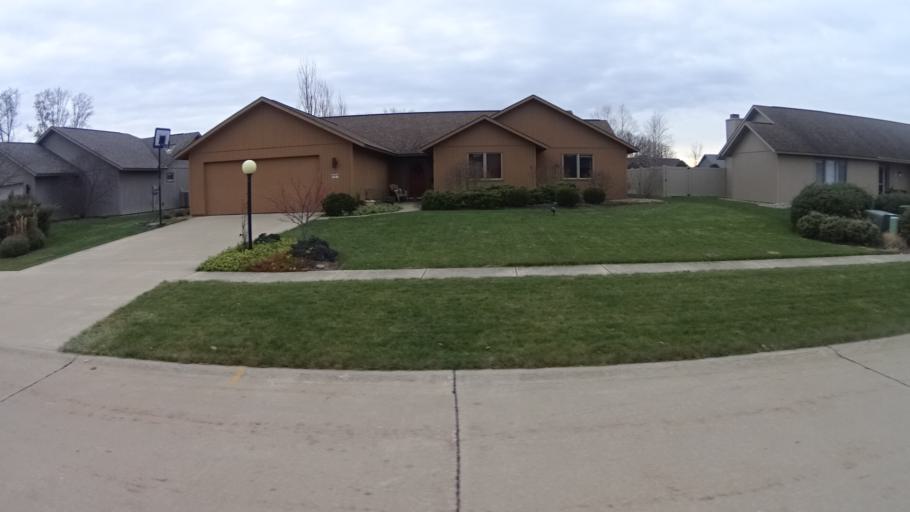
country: US
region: Ohio
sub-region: Lorain County
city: North Ridgeville
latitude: 41.3611
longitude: -81.9837
